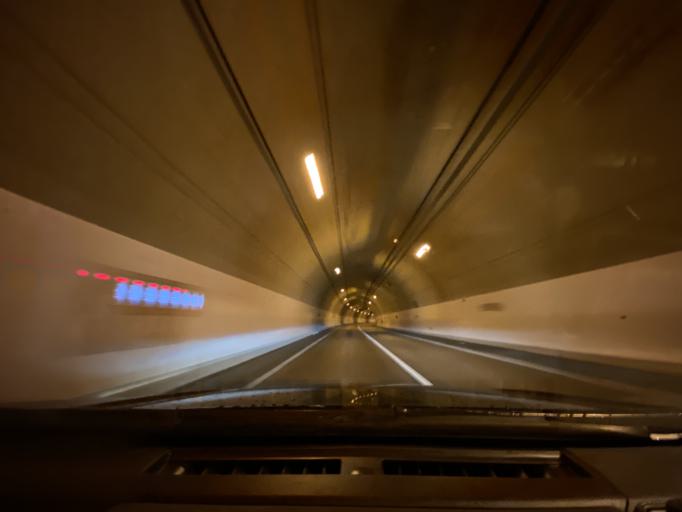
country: JP
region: Hokkaido
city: Ishikari
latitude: 43.4684
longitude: 141.3980
